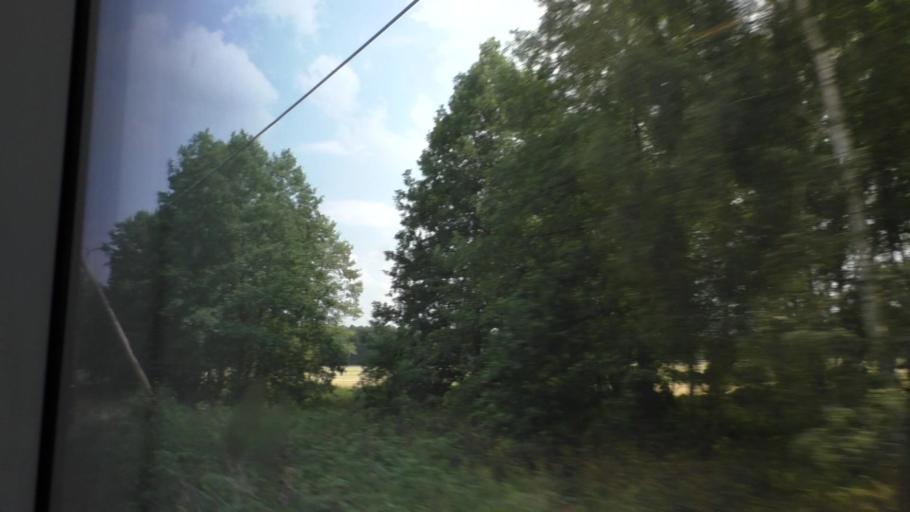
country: DE
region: Brandenburg
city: Storkow
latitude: 52.2803
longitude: 13.8547
